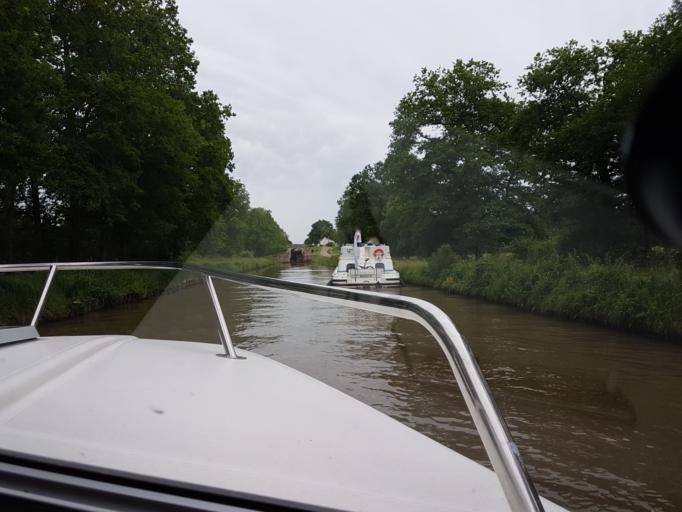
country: FR
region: Bourgogne
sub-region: Departement de la Nievre
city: Clamecy
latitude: 47.3807
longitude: 3.6028
